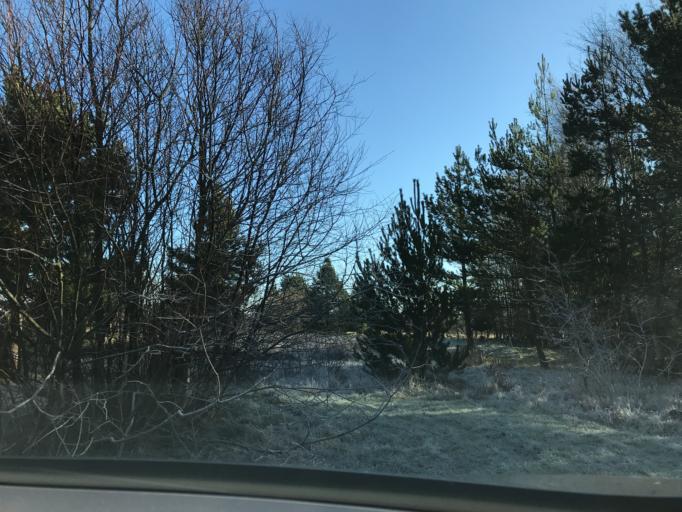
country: DK
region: South Denmark
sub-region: Varde Kommune
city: Oksbol
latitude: 55.7742
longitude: 8.2452
